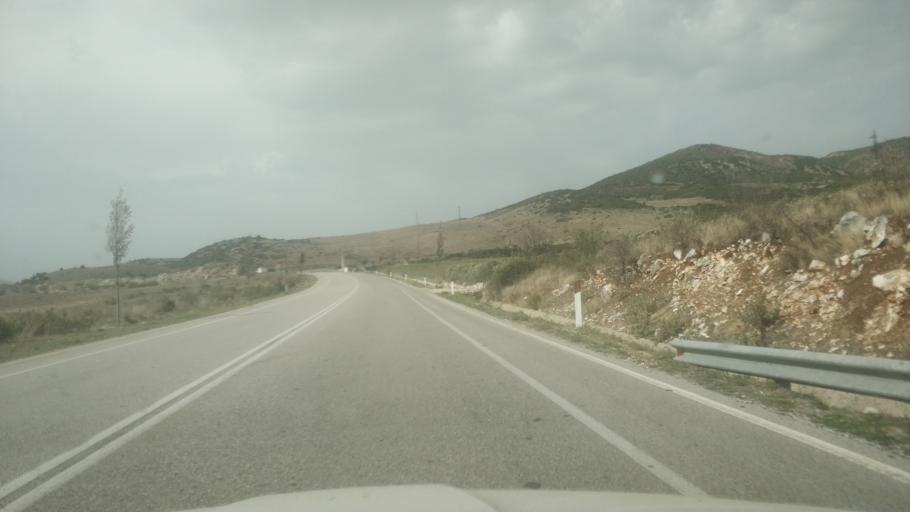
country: AL
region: Gjirokaster
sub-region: Rrethi i Tepelenes
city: Memaliaj
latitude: 40.3619
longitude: 19.9277
